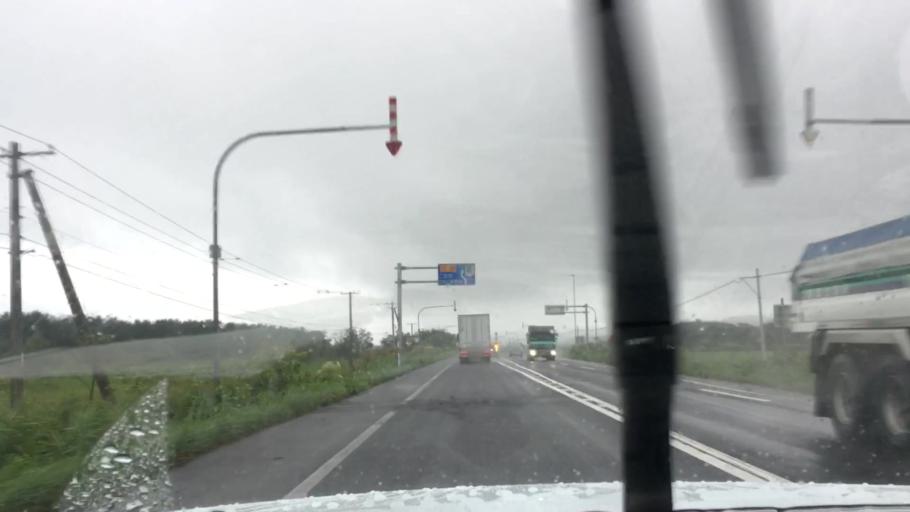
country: JP
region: Hokkaido
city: Niseko Town
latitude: 42.4203
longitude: 140.3126
